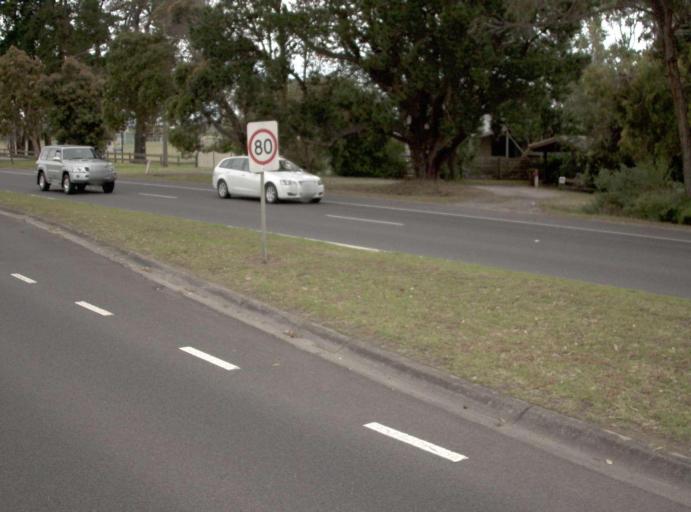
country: AU
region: Victoria
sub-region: Casey
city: Tooradin
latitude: -38.2097
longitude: 145.3773
